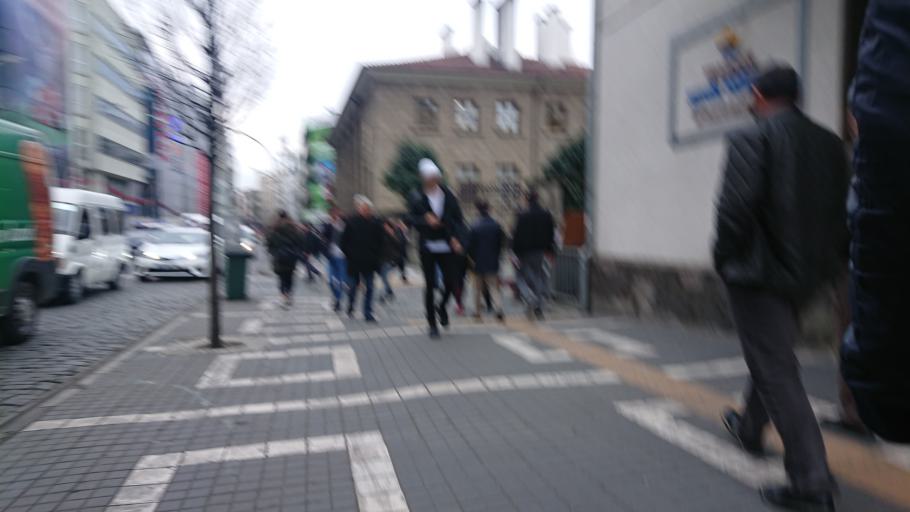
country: TR
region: Trabzon
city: Trabzon
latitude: 41.0059
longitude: 39.7281
